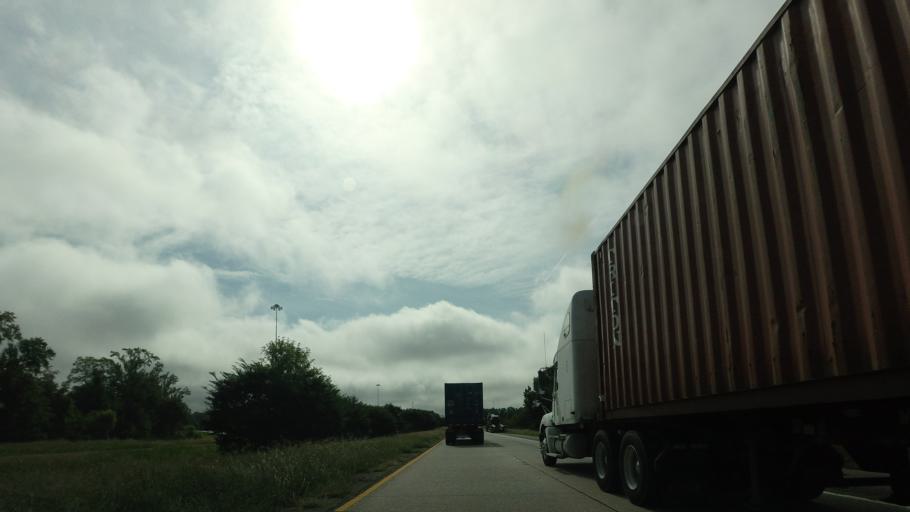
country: US
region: Georgia
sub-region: Bibb County
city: Macon
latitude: 32.8024
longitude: -83.5713
